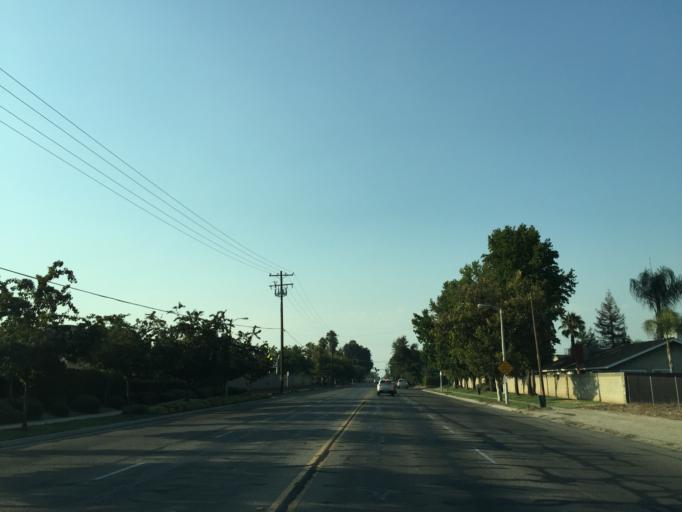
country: US
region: California
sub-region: Tulare County
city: Visalia
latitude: 36.3478
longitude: -119.2789
